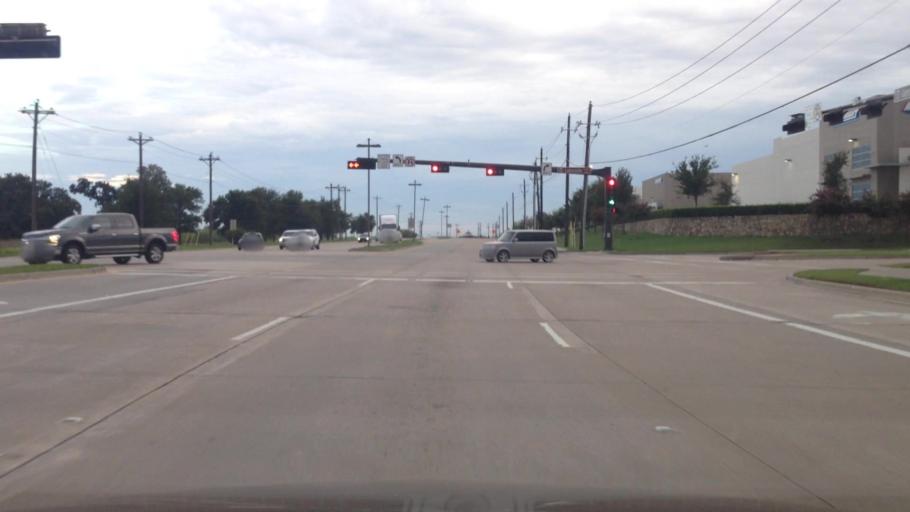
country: US
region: Texas
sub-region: Dallas County
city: Coppell
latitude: 32.9953
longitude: -97.0457
